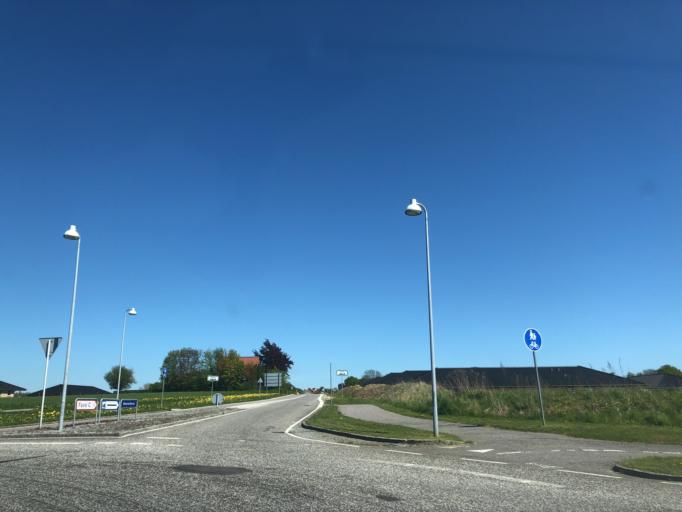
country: DK
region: Zealand
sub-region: Faxe Kommune
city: Fakse
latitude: 55.2555
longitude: 12.0986
